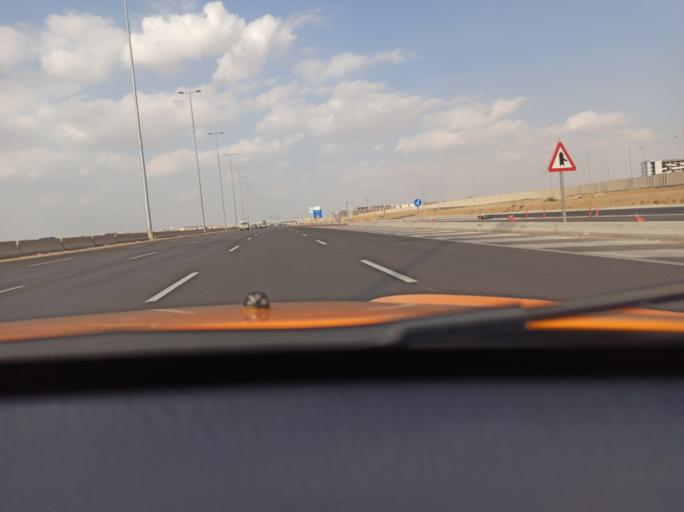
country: EG
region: Eastern Province
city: Bilbays
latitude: 30.2014
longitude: 31.6630
